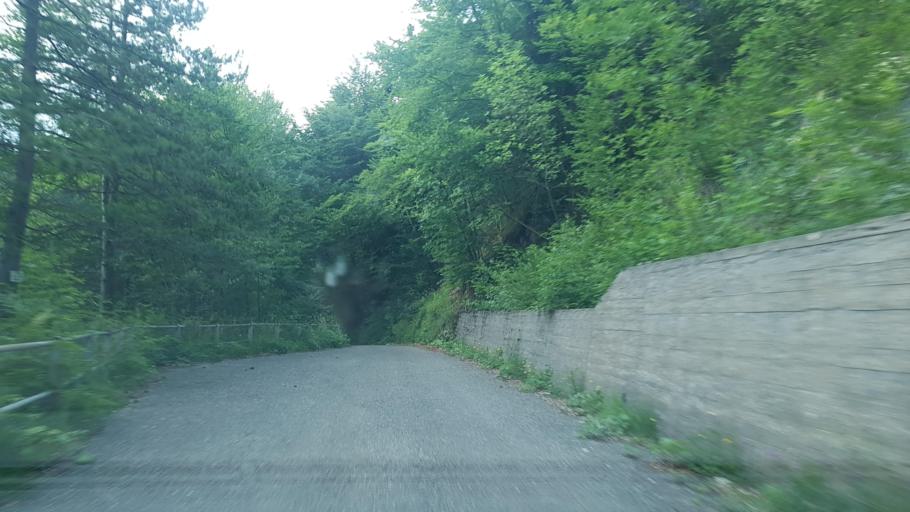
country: IT
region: Friuli Venezia Giulia
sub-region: Provincia di Udine
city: Paularo
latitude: 46.4765
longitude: 13.0972
